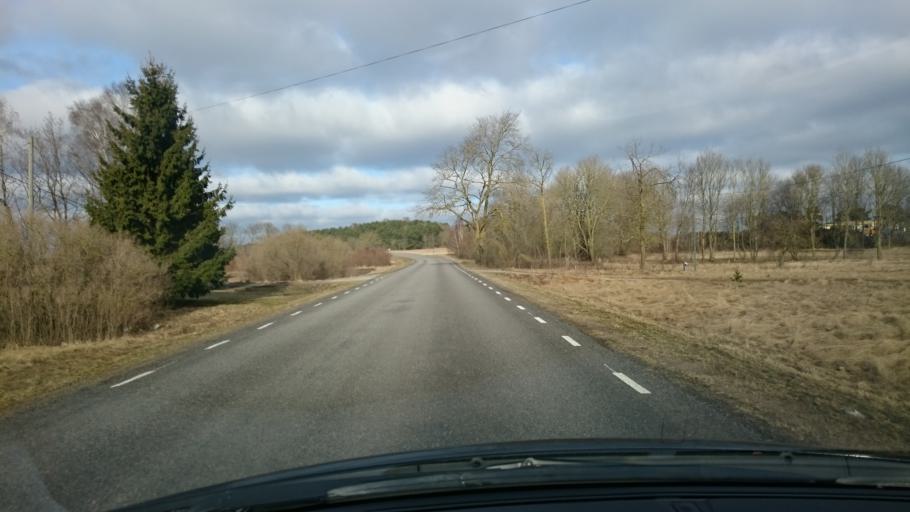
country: EE
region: Harju
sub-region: Keila linn
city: Keila
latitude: 59.3373
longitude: 24.3719
